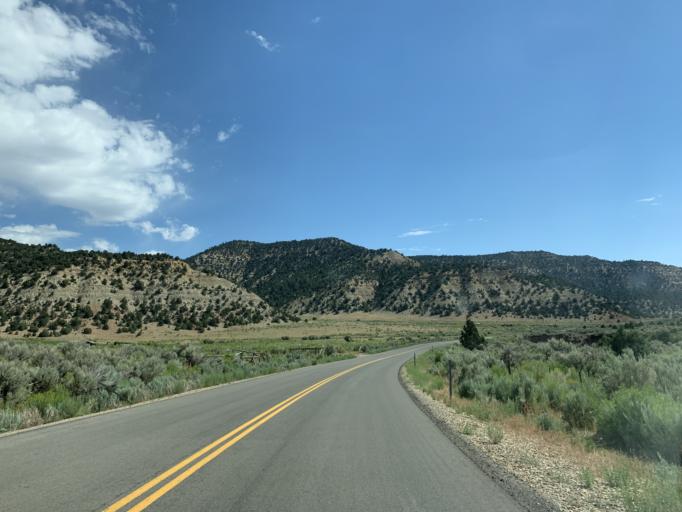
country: US
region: Utah
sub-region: Carbon County
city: East Carbon City
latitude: 39.7729
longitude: -110.5153
